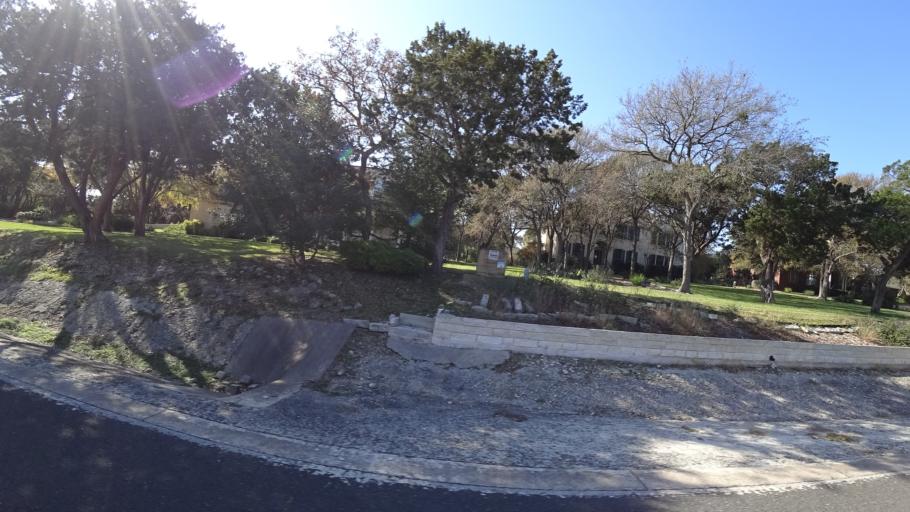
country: US
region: Texas
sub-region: Williamson County
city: Anderson Mill
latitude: 30.3819
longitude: -97.8278
